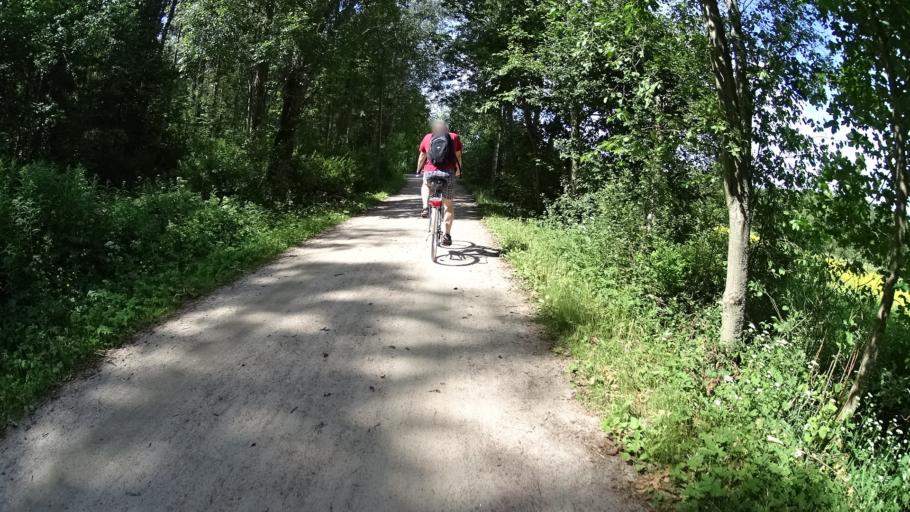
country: FI
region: Uusimaa
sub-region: Helsinki
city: Helsinki
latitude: 60.2699
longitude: 24.9122
